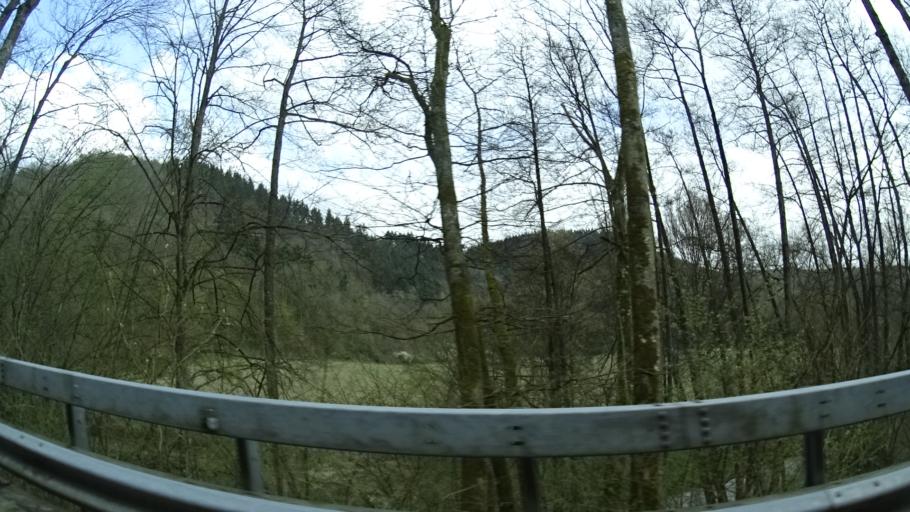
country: DE
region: Rheinland-Pfalz
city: Heinzenberg
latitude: 49.8332
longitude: 7.4823
